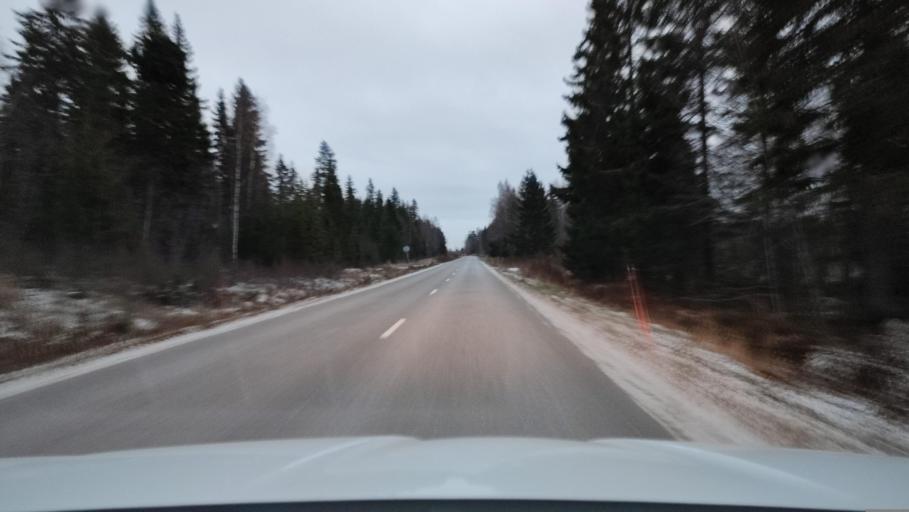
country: FI
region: Ostrobothnia
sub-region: Vaasa
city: Replot
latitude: 63.2372
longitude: 21.3937
